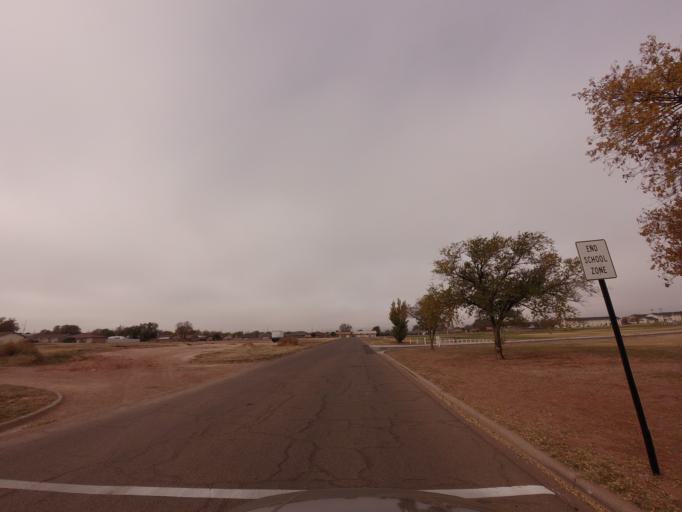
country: US
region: New Mexico
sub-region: Curry County
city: Clovis
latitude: 34.4110
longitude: -103.2249
